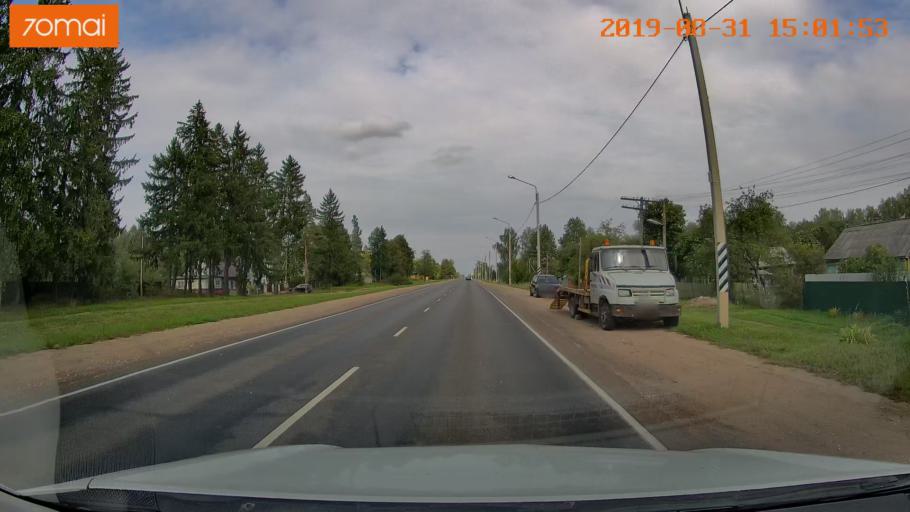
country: RU
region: Kaluga
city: Spas-Demensk
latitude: 54.3421
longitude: 34.0655
